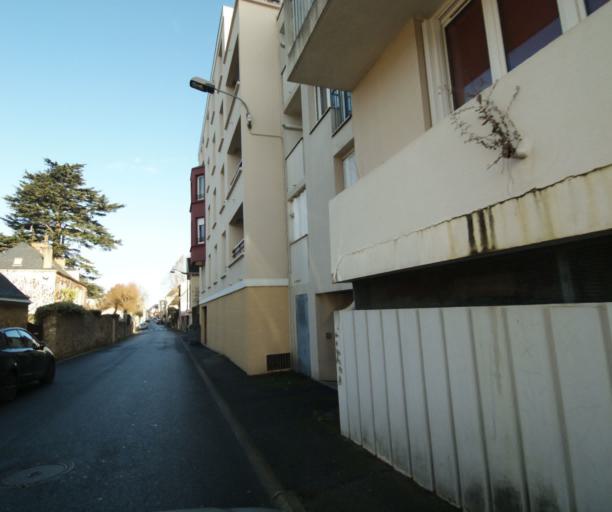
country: FR
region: Pays de la Loire
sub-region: Departement de la Sarthe
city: Coulaines
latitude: 48.0210
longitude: 0.2045
